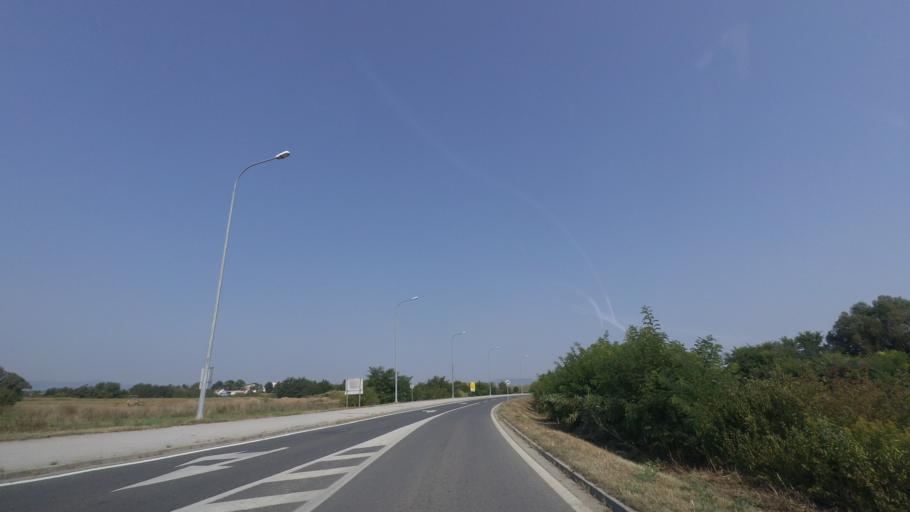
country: HR
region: Pozesko-Slavonska
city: Vidovci
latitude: 45.3385
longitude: 17.7082
